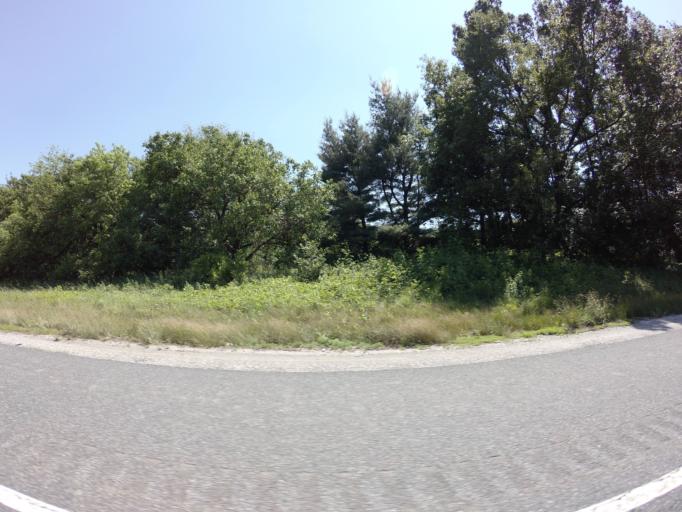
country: US
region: Maryland
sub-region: Carroll County
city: Mount Airy
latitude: 39.3470
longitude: -77.0911
